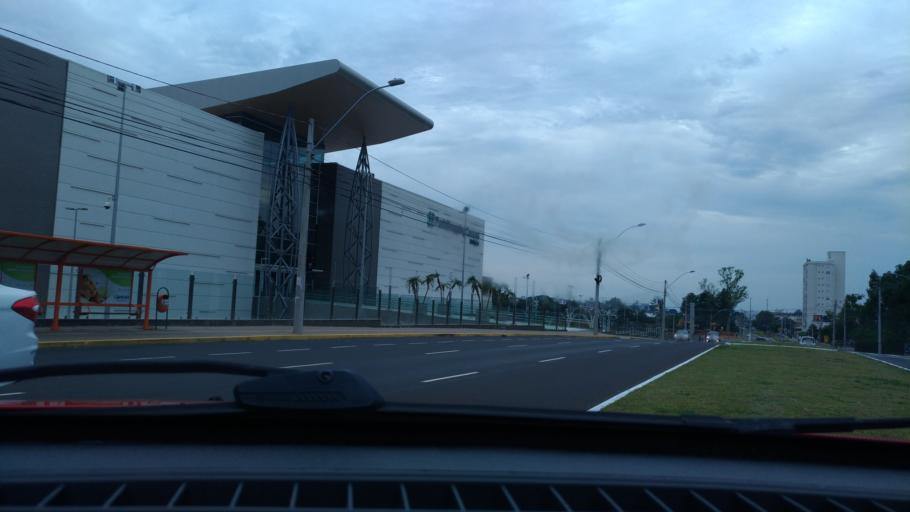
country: BR
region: Rio Grande do Sul
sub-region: Canoas
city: Canoas
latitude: -29.9155
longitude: -51.1658
